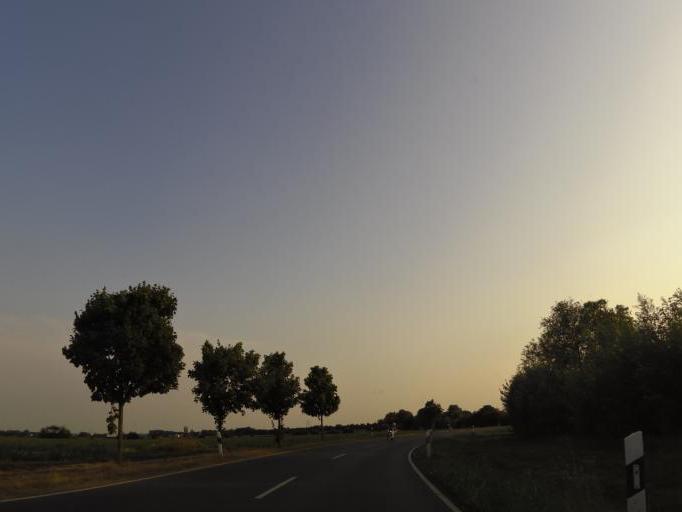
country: DE
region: Hesse
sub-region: Regierungsbezirk Darmstadt
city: Buttelborn
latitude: 49.9148
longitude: 8.5254
